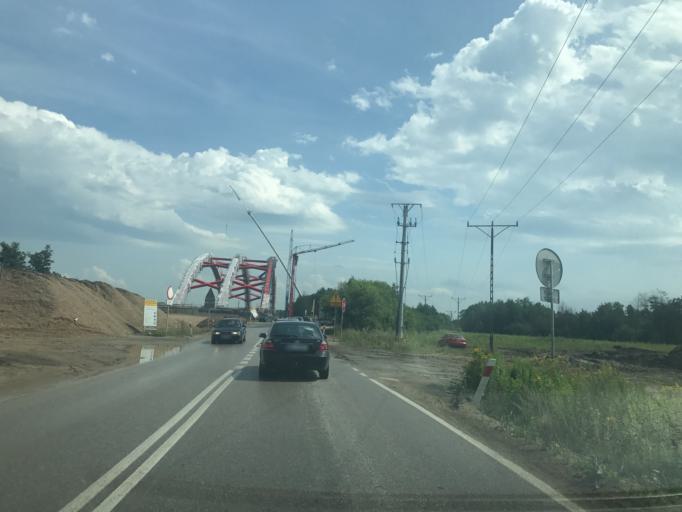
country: PL
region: Warmian-Masurian Voivodeship
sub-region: Powiat ostrodzki
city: Ostroda
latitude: 53.7145
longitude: 19.9605
